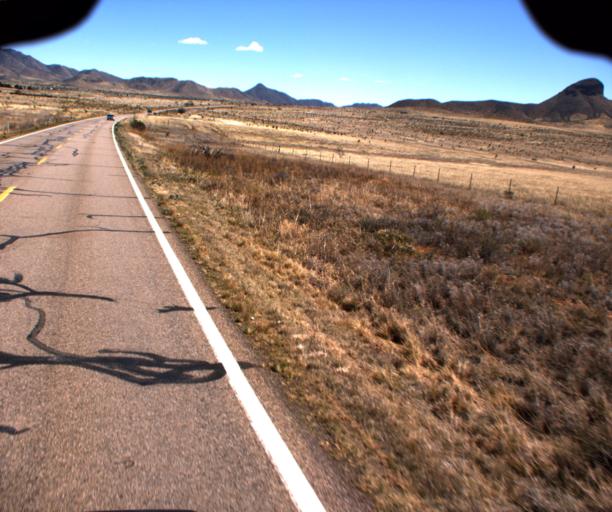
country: US
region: Arizona
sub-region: Cochise County
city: Huachuca City
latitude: 31.7222
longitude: -110.5342
